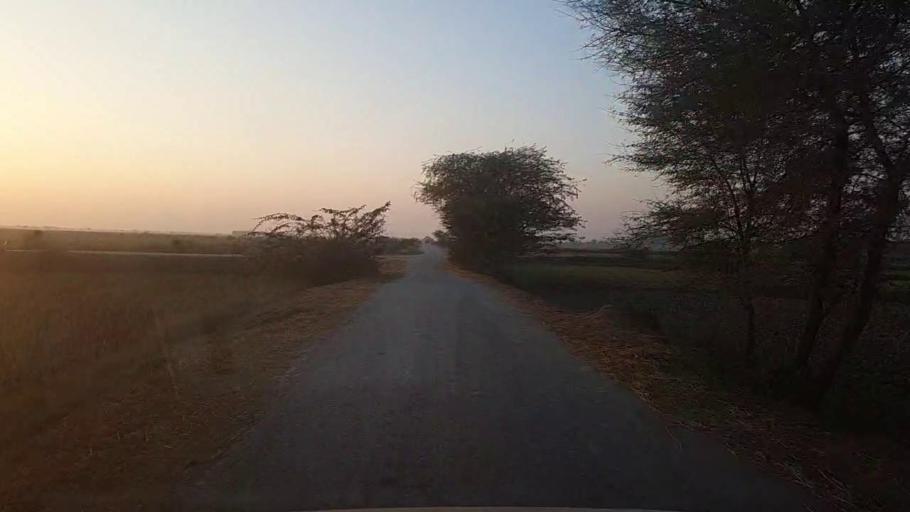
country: PK
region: Sindh
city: Khairpur Nathan Shah
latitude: 27.1538
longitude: 67.7295
